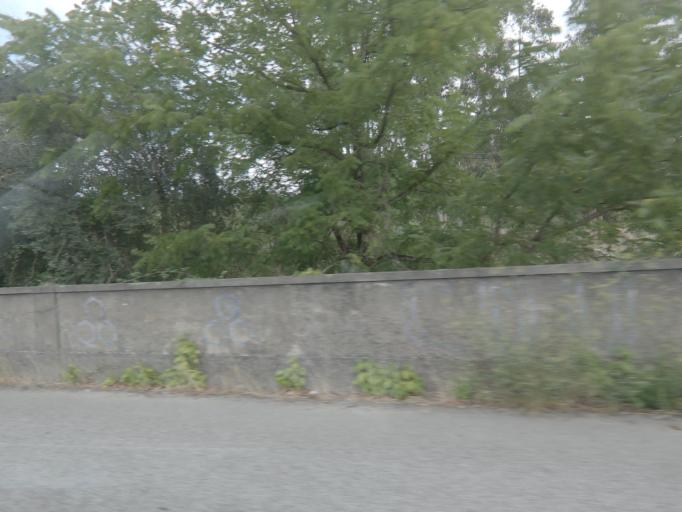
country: PT
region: Coimbra
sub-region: Condeixa-A-Nova
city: Condeixa-a-Nova
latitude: 40.1382
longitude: -8.4682
